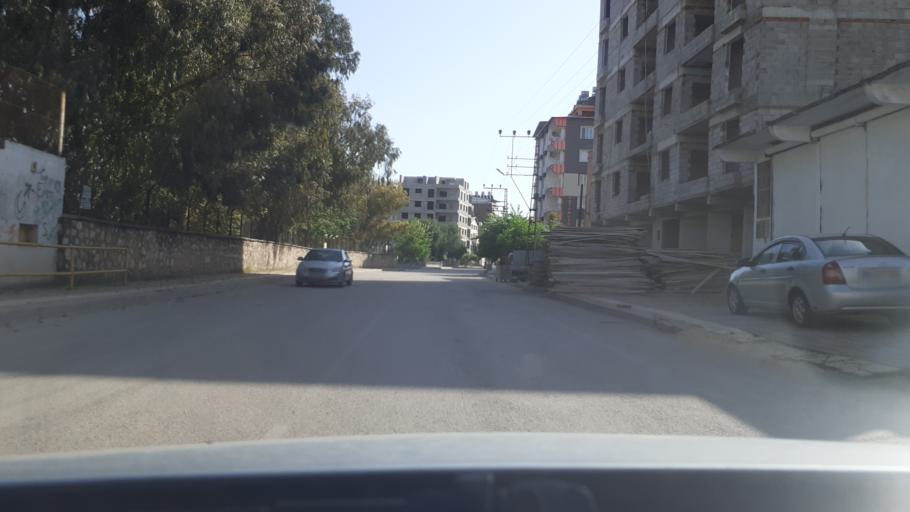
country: TR
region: Hatay
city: Kirikhan
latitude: 36.4936
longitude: 36.3672
